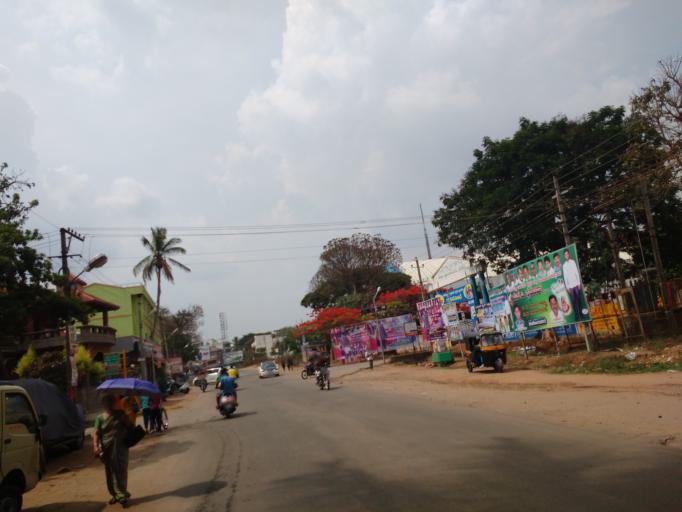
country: IN
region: Karnataka
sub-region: Hassan
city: Hassan
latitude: 13.0186
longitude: 76.1004
